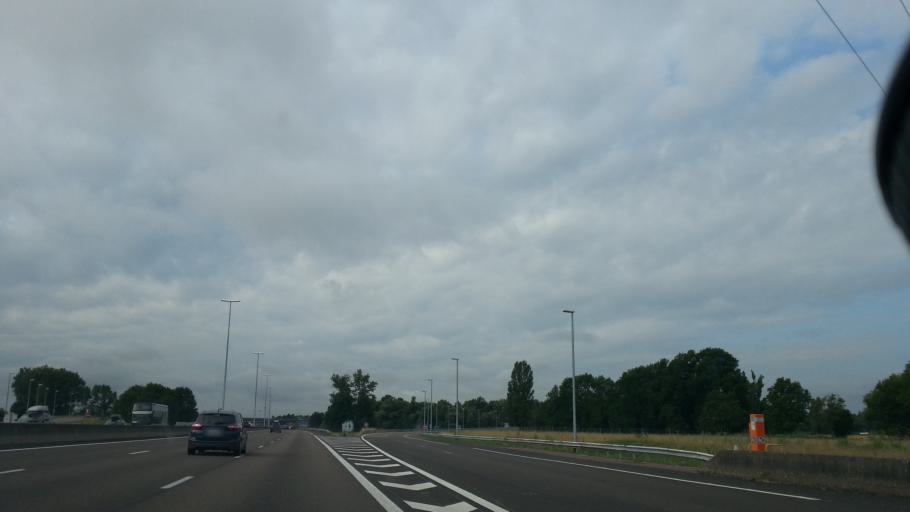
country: FR
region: Bourgogne
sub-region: Departement de la Cote-d'Or
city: Beaune
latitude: 47.0357
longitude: 4.8809
